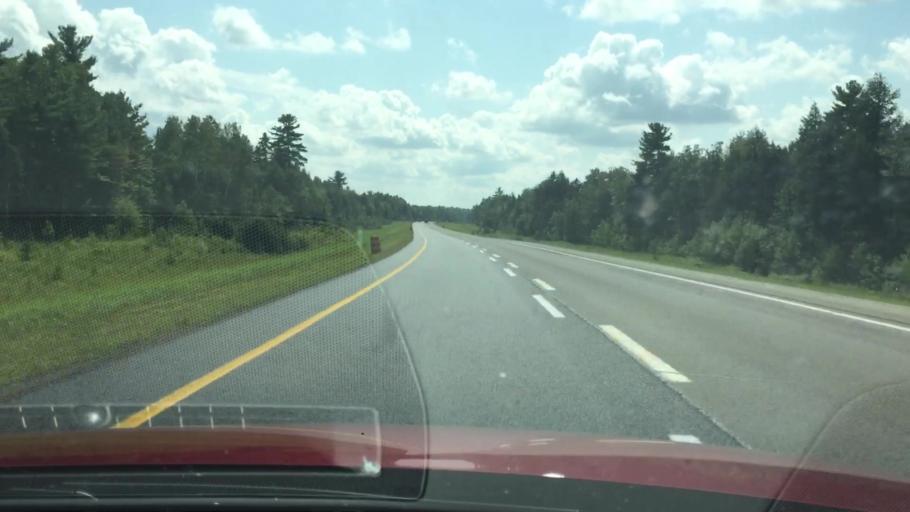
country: US
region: Maine
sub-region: Penobscot County
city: Medway
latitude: 45.6971
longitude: -68.4870
